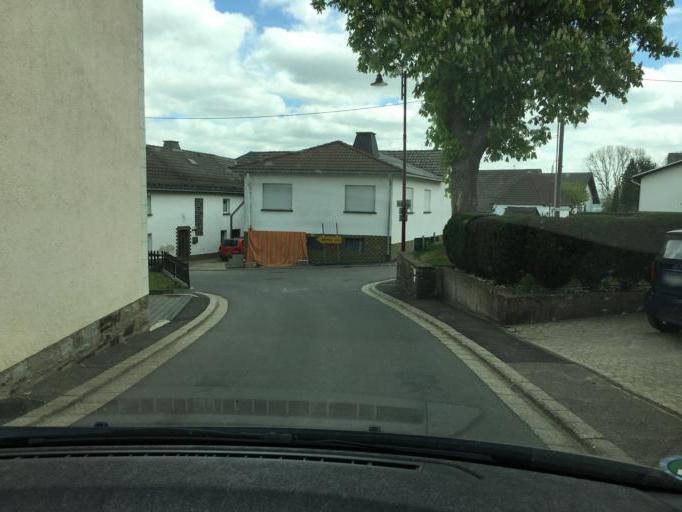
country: DE
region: Rheinland-Pfalz
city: Lind
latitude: 50.4940
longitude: 6.9375
